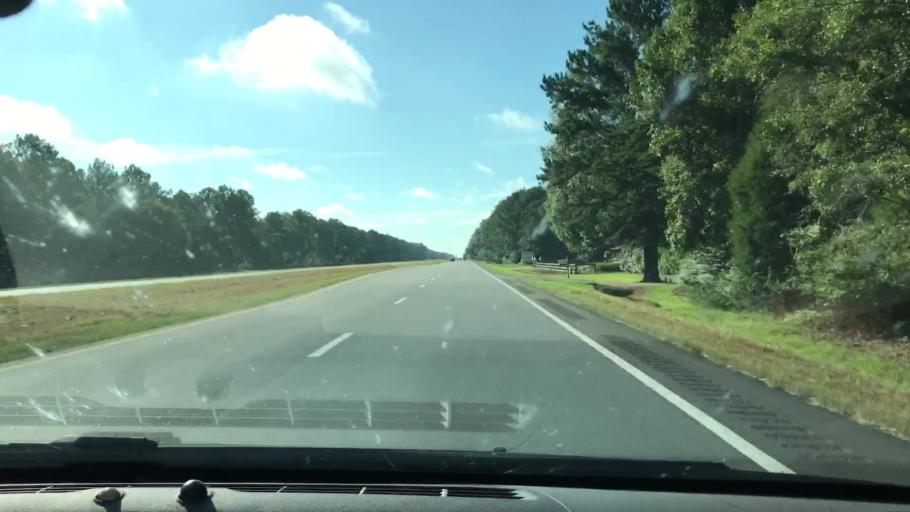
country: US
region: Georgia
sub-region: Lee County
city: Leesburg
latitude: 31.6863
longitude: -84.3071
